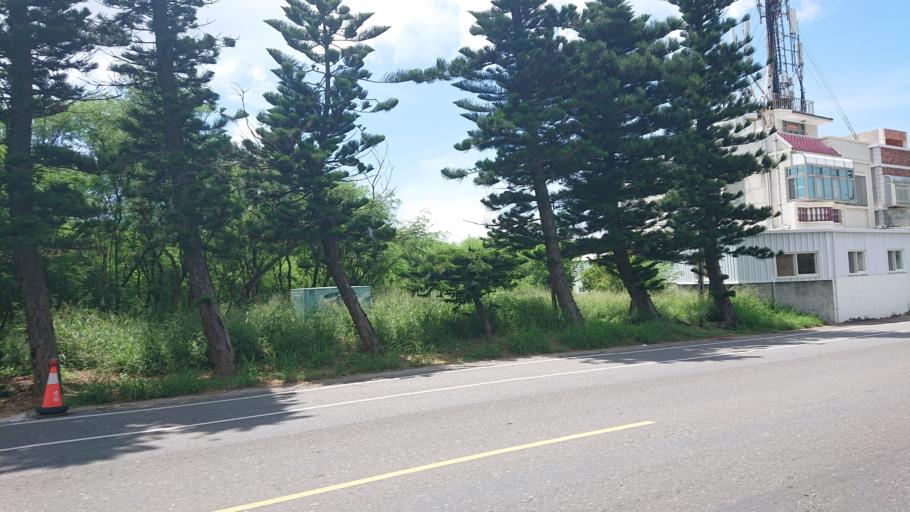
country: TW
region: Taiwan
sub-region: Penghu
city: Ma-kung
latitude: 23.5930
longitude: 119.6131
